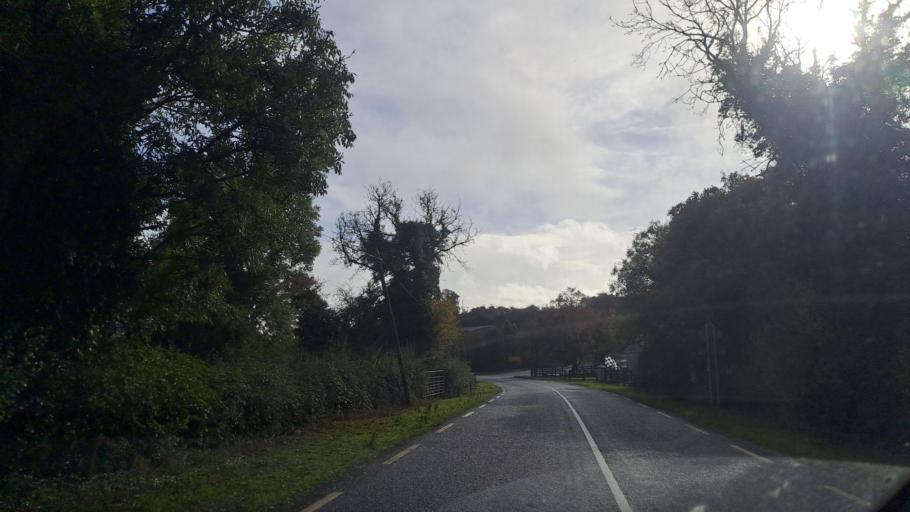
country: IE
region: Ulster
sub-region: County Monaghan
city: Carrickmacross
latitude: 53.9066
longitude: -6.7016
